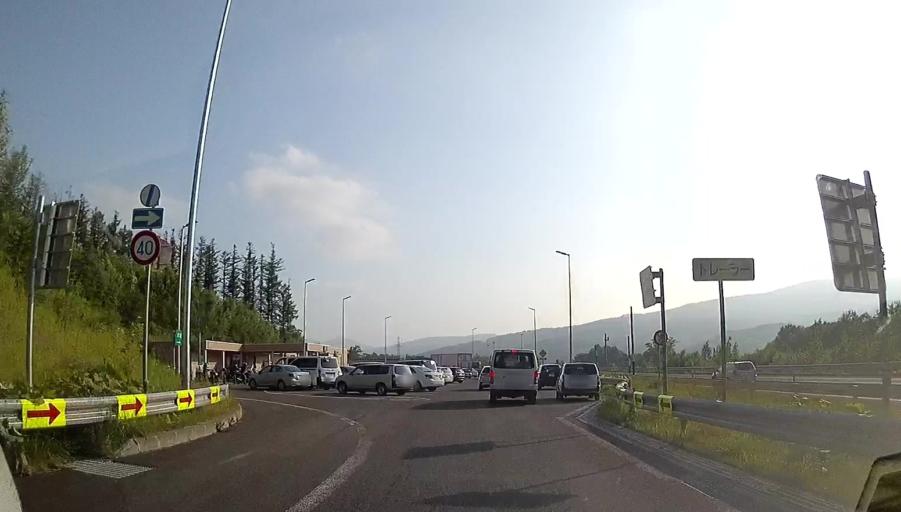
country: JP
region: Hokkaido
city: Shimo-furano
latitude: 43.0061
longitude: 142.4169
